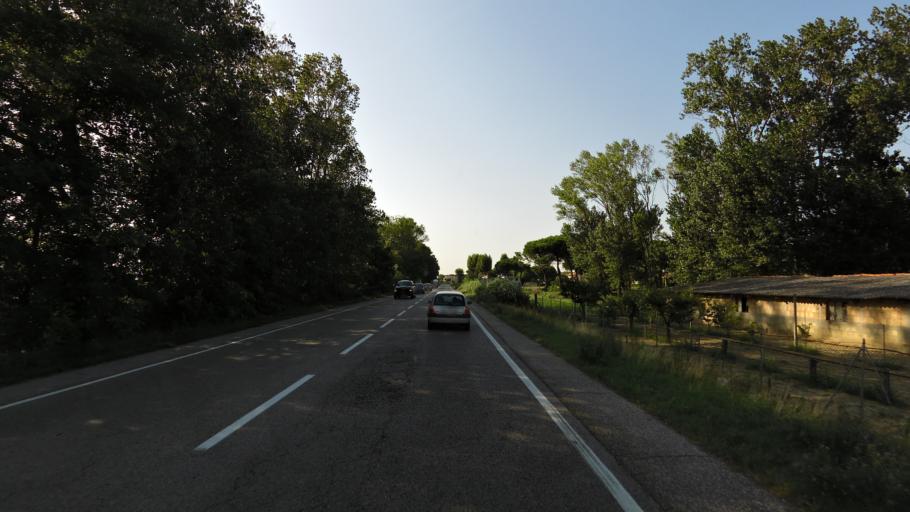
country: IT
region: Emilia-Romagna
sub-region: Provincia di Ravenna
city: Cervia
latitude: 44.2469
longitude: 12.3494
